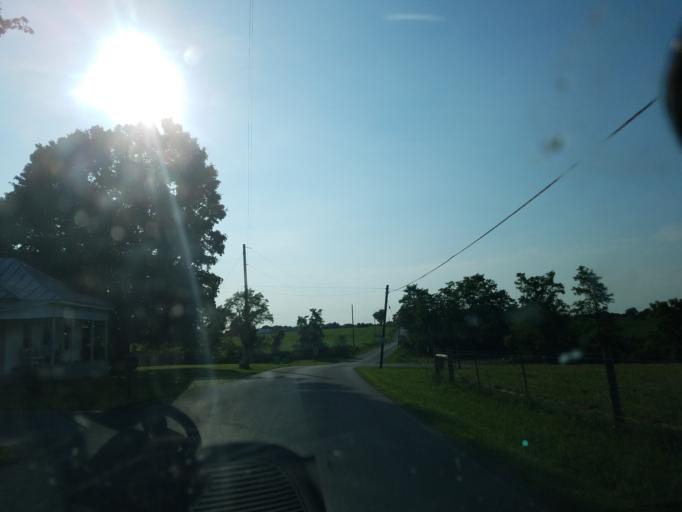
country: US
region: Ohio
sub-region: Adams County
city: West Union
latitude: 38.8786
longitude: -83.4891
